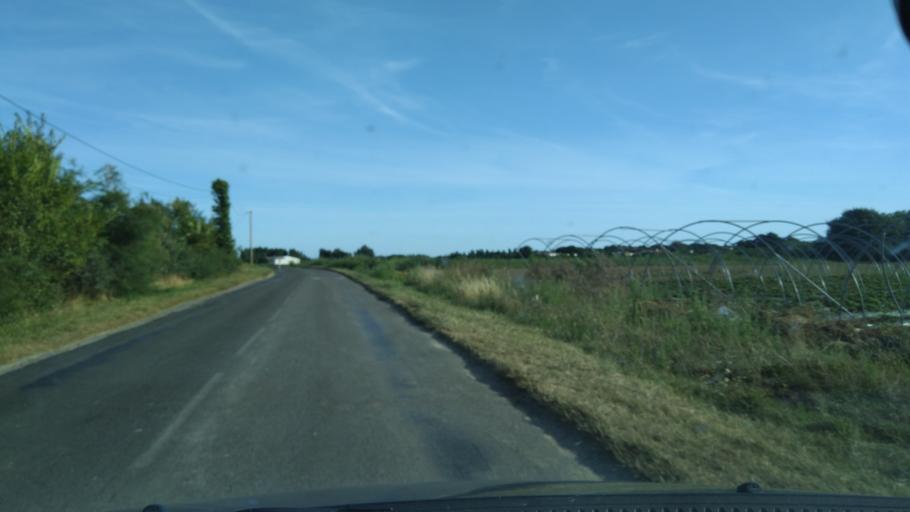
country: FR
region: Poitou-Charentes
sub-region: Departement de la Charente-Maritime
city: Dolus-d'Oleron
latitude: 45.9366
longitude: -1.3382
